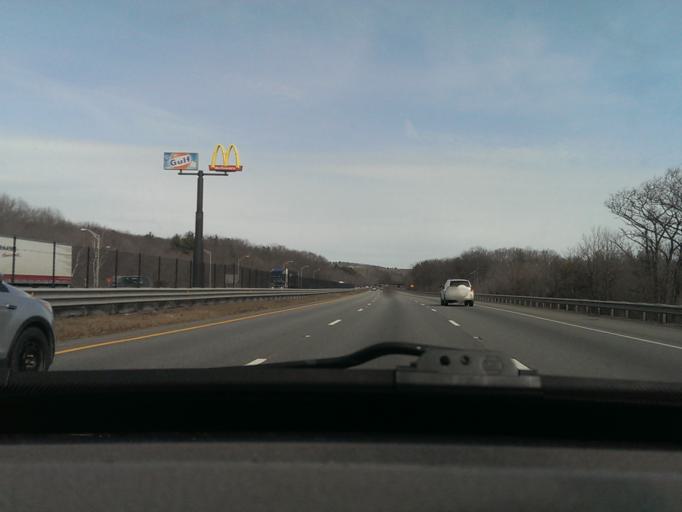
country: US
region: Massachusetts
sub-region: Worcester County
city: Charlton
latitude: 42.1558
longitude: -71.9631
